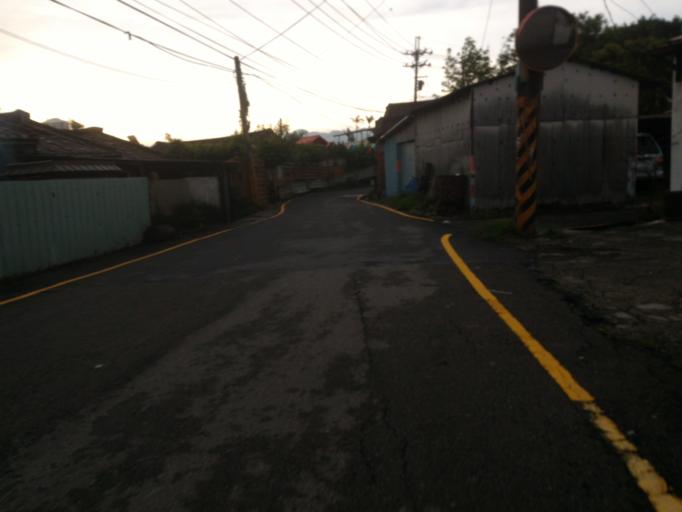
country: TW
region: Taipei
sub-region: Taipei
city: Banqiao
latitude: 24.9758
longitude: 121.4185
